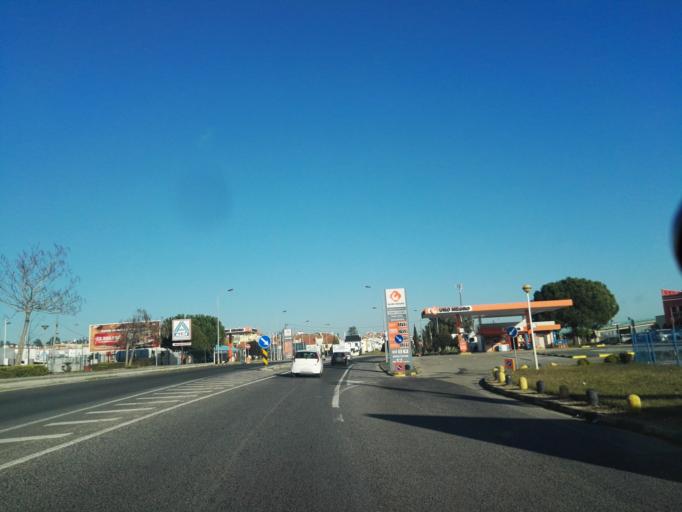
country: PT
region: Lisbon
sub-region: Azambuja
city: Azambuja
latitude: 39.0653
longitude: -8.8773
